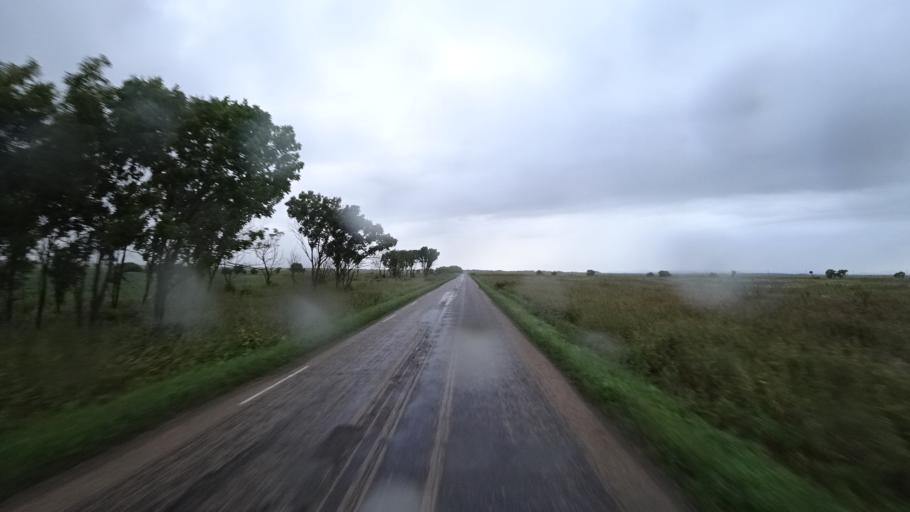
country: RU
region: Primorskiy
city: Chernigovka
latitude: 44.3791
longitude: 132.5297
